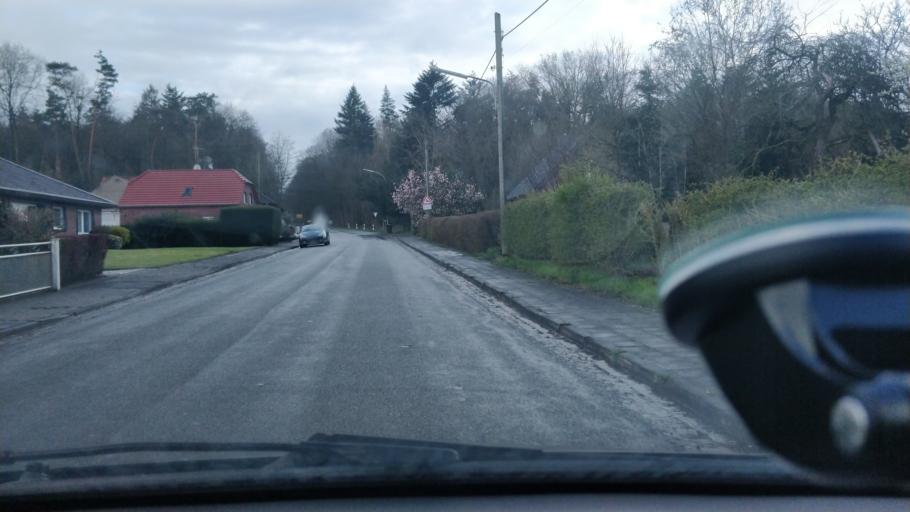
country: DE
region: North Rhine-Westphalia
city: Rees
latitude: 51.6942
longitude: 6.3709
